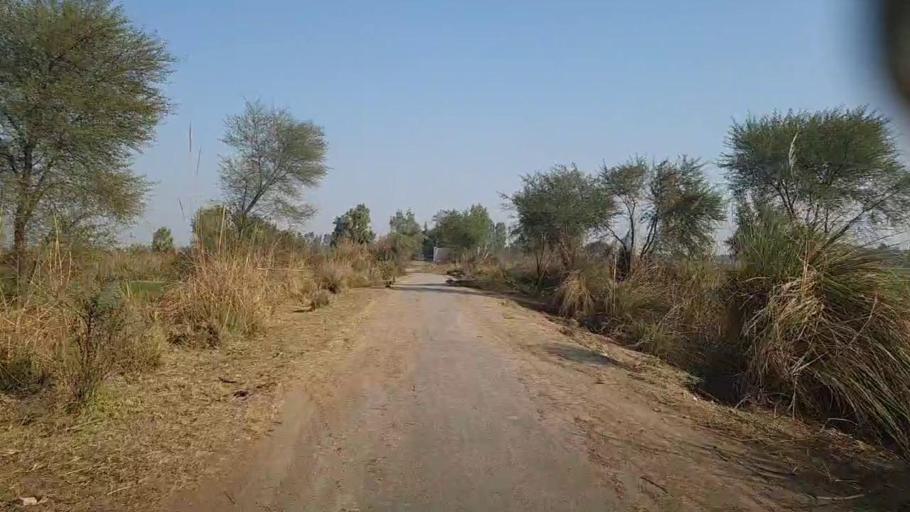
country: PK
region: Sindh
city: Mirpur Mathelo
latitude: 27.8769
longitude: 69.6146
